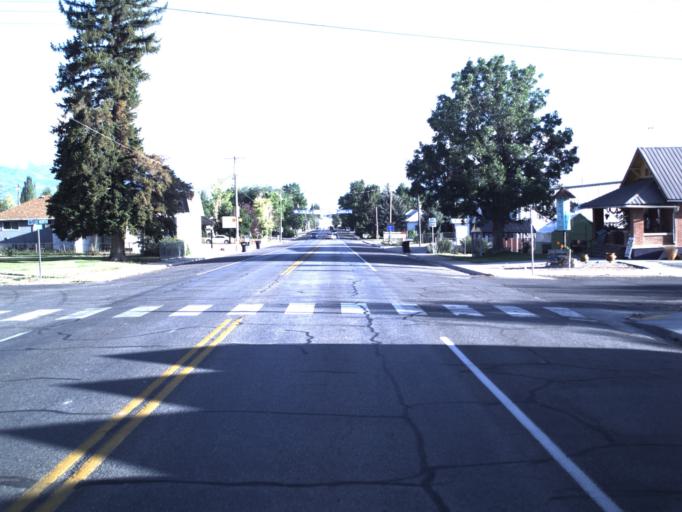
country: US
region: Utah
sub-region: Sanpete County
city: Fairview
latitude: 39.6315
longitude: -111.4393
